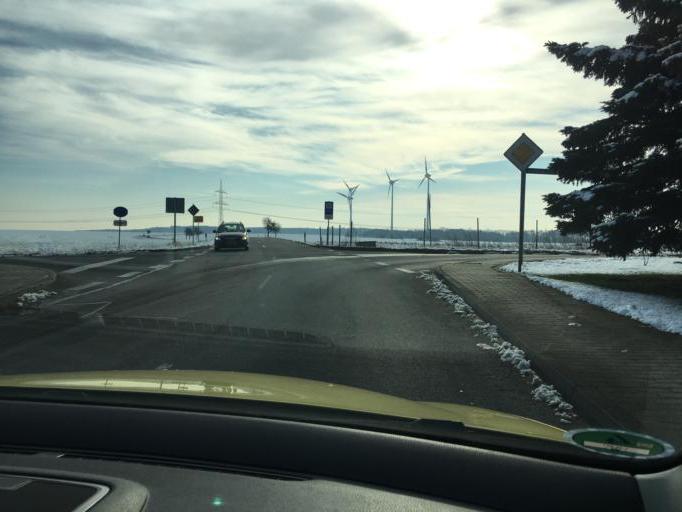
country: DE
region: Saxony
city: Geithain
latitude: 51.0993
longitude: 12.6959
